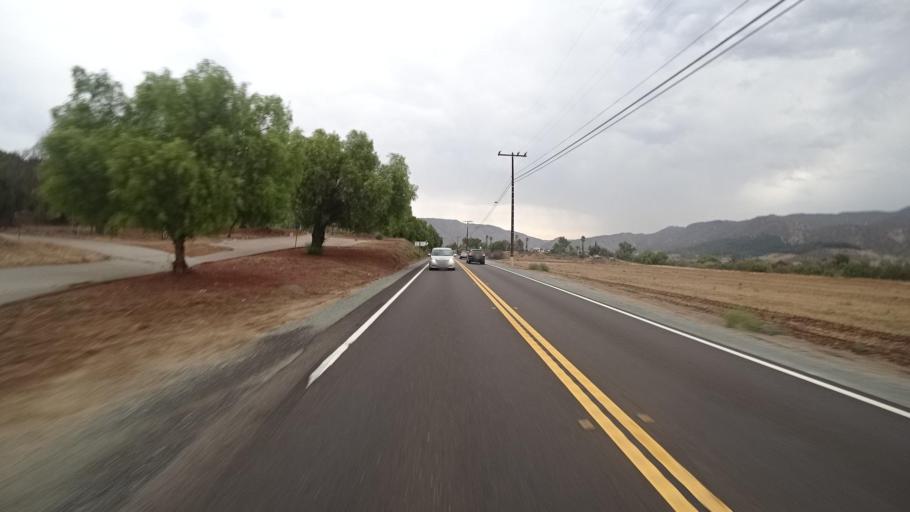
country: US
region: California
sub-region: San Diego County
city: San Pasqual
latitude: 33.0888
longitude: -116.9801
